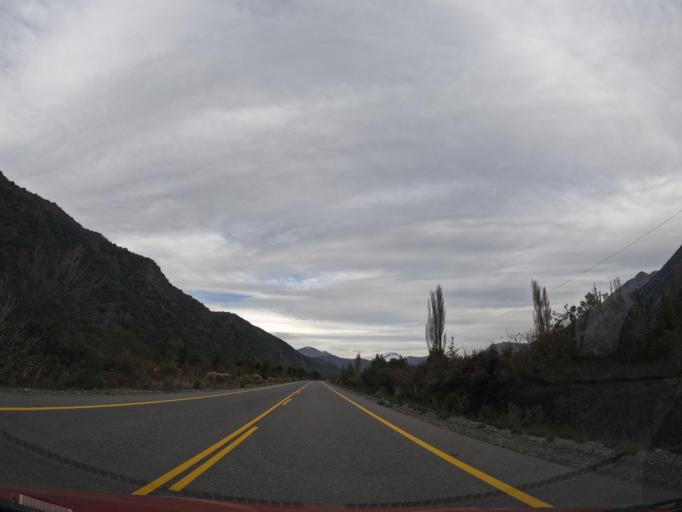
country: CL
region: Maule
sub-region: Provincia de Linares
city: Colbun
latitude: -35.7292
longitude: -71.0170
